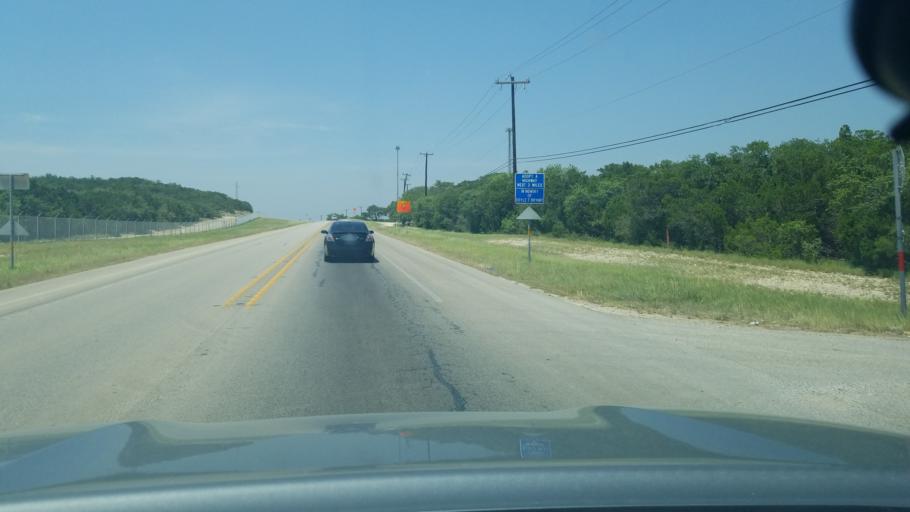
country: US
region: Texas
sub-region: Bexar County
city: Timberwood Park
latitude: 29.6974
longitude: -98.5212
